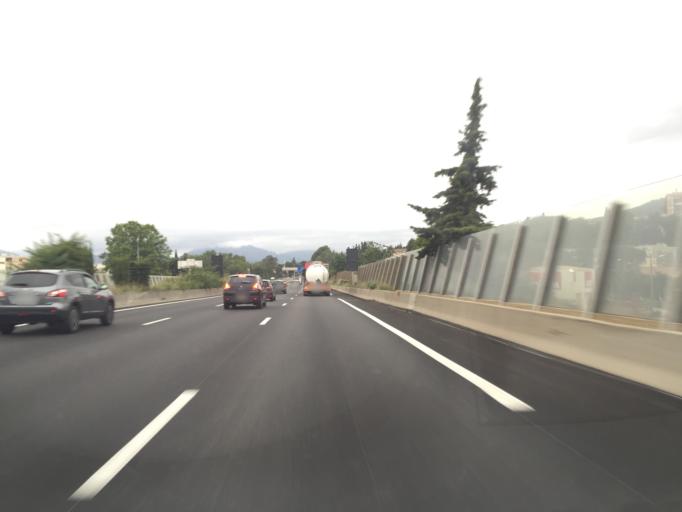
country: FR
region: Provence-Alpes-Cote d'Azur
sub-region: Departement des Alpes-Maritimes
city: Mandelieu-la-Napoule
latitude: 43.5608
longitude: 6.9678
